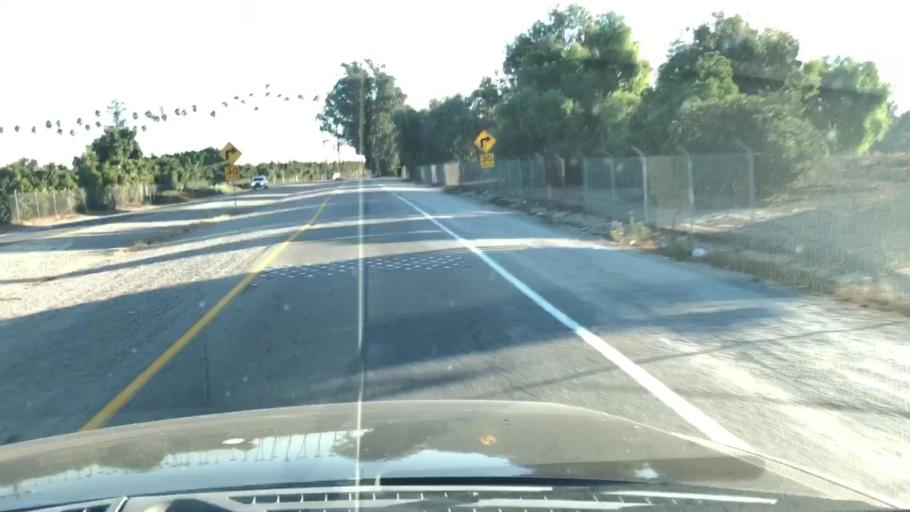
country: US
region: California
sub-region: Ventura County
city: Saticoy
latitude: 34.2656
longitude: -119.1276
